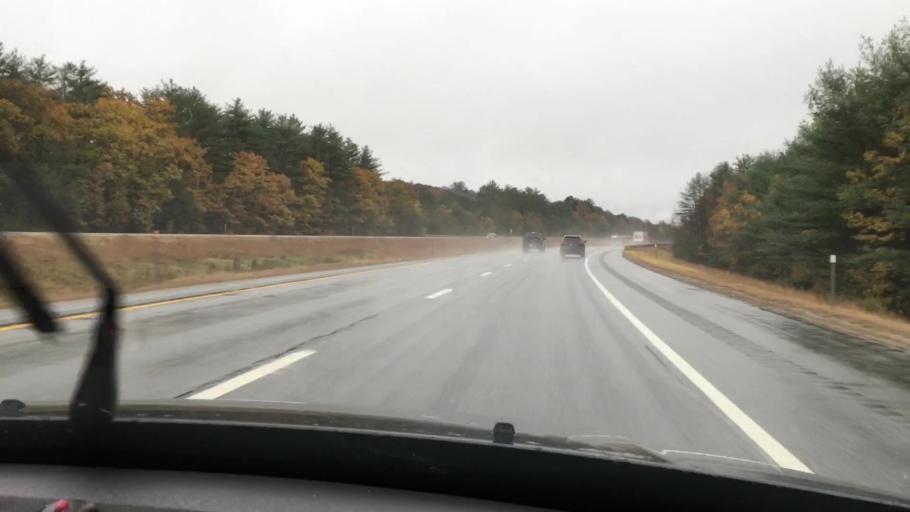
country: US
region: New Hampshire
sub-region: Grafton County
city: Ashland
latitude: 43.6455
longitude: -71.6474
